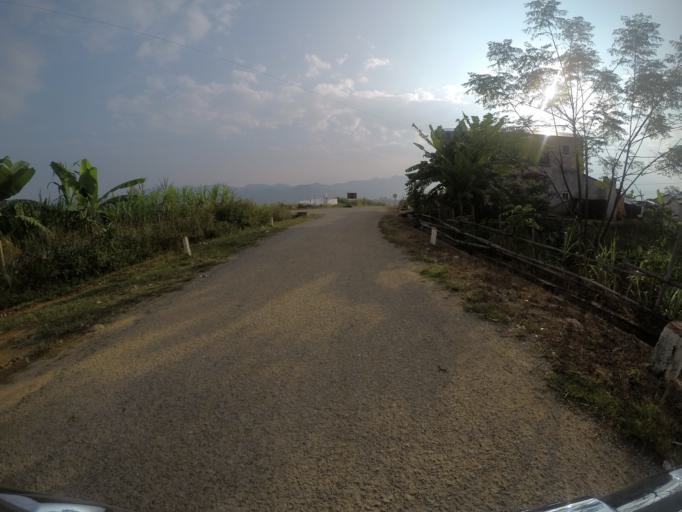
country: VN
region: Lao Cai
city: Sa Pa
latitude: 22.1758
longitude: 103.7847
